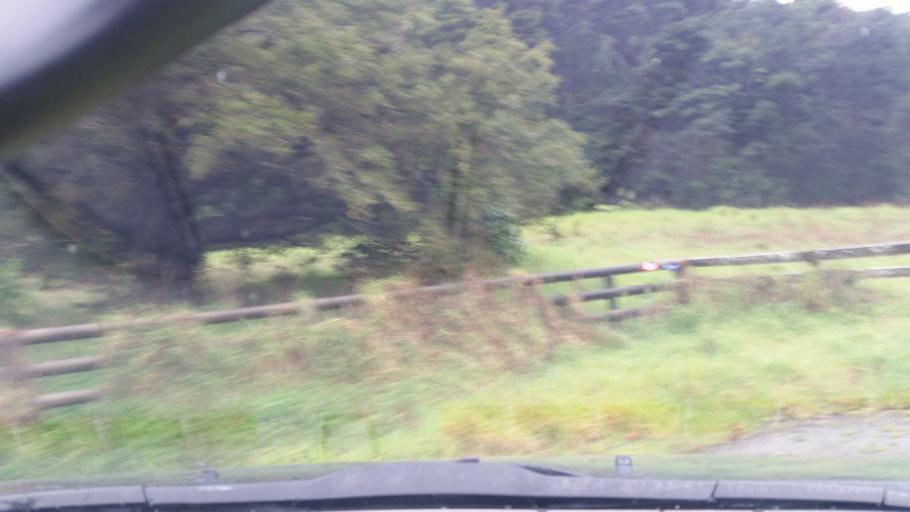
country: NZ
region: Auckland
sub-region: Auckland
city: Wellsford
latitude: -36.1010
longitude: 174.5058
